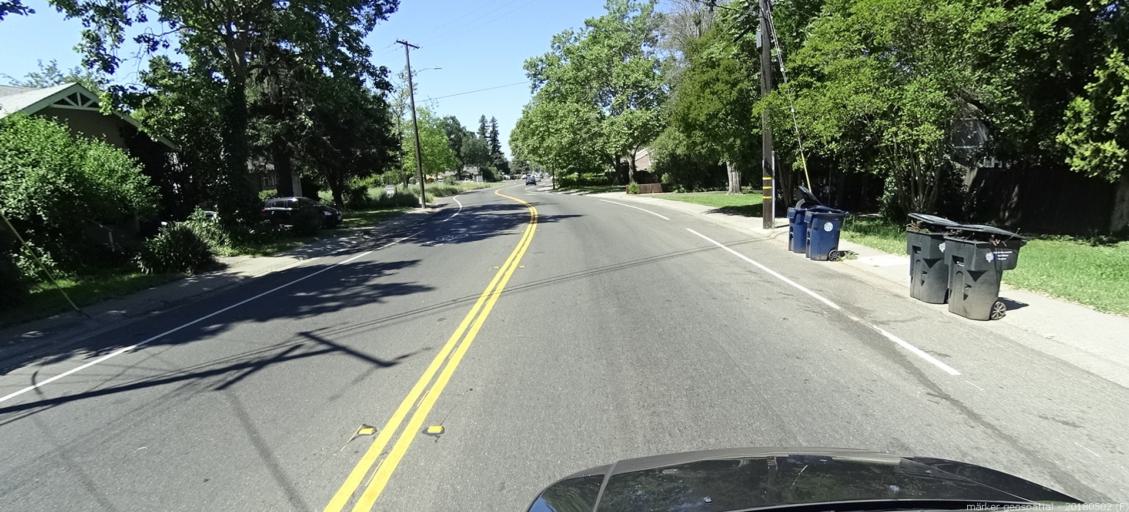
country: US
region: California
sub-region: Sacramento County
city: Arden-Arcade
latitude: 38.6263
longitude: -121.4289
